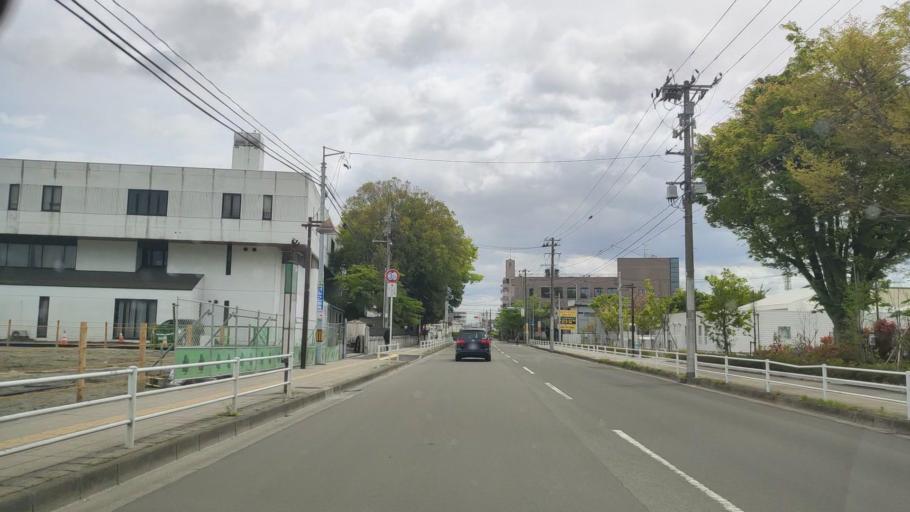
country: JP
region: Miyagi
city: Sendai-shi
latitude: 38.2602
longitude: 140.9076
